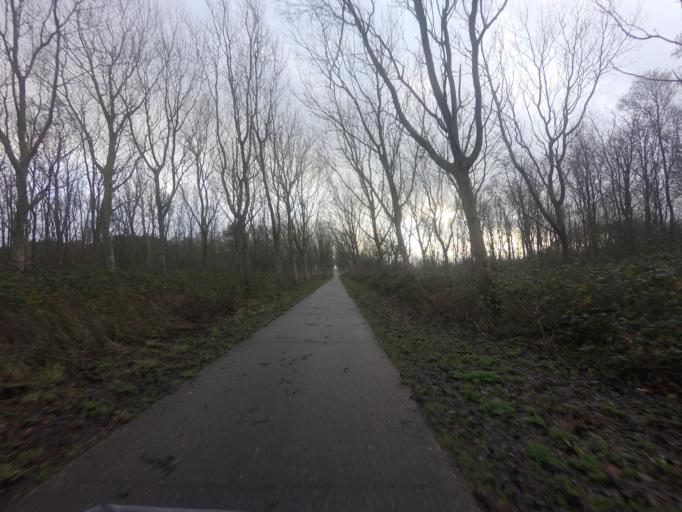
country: NL
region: North Holland
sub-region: Gemeente Texel
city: Den Burg
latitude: 53.1615
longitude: 4.8522
